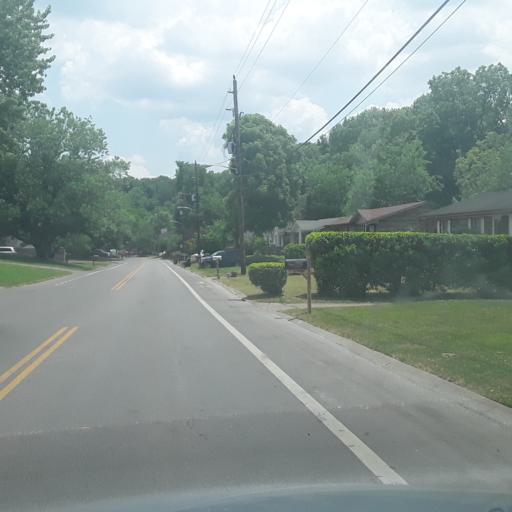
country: US
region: Tennessee
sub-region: Williamson County
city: Brentwood Estates
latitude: 36.0500
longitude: -86.6947
